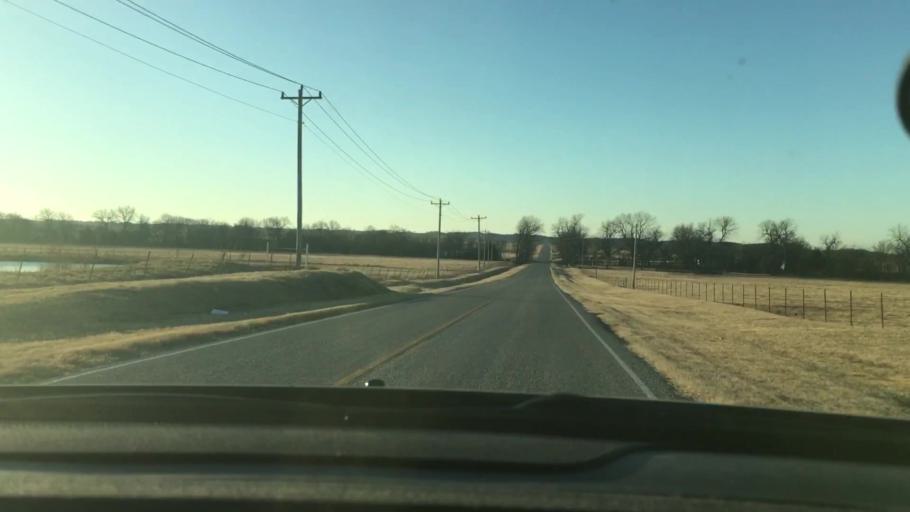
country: US
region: Oklahoma
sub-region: Murray County
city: Davis
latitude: 34.4866
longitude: -97.0906
